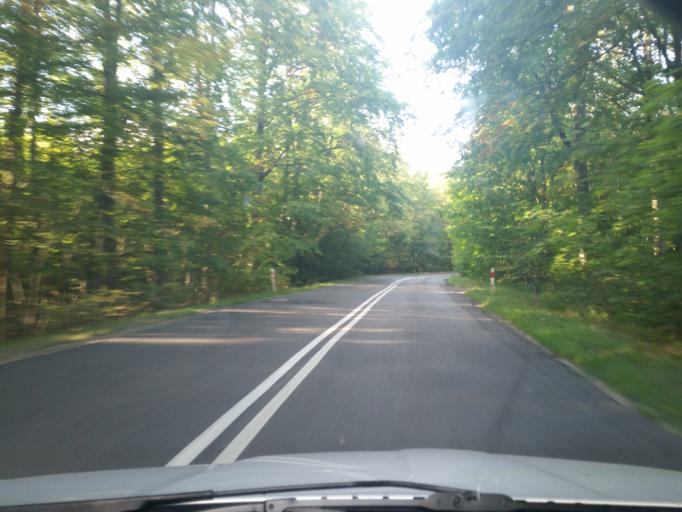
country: PL
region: Pomeranian Voivodeship
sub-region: Powiat chojnicki
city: Chojnice
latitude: 53.7329
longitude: 17.4759
